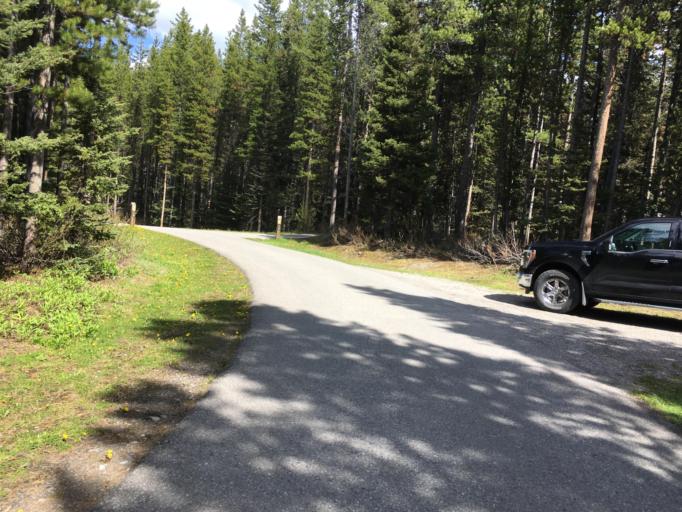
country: CA
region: Alberta
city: Canmore
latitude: 50.6257
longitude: -115.1013
